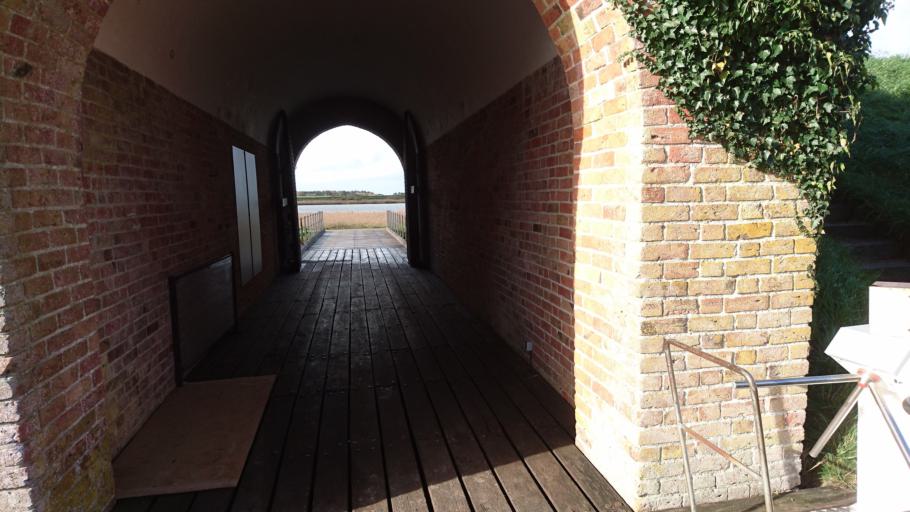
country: DK
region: Central Jutland
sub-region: Holstebro Kommune
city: Vinderup
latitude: 56.6398
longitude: 8.7821
